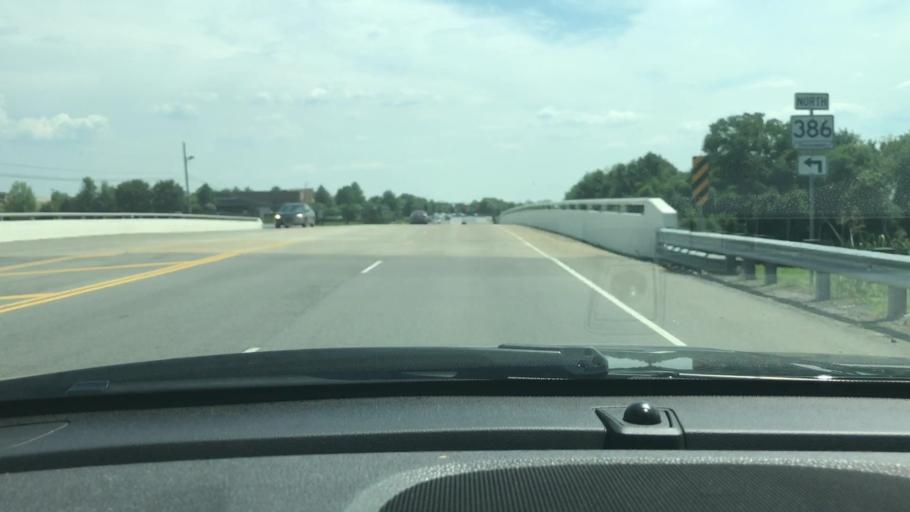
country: US
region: Tennessee
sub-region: Sumner County
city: Hendersonville
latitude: 36.3333
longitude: -86.5936
